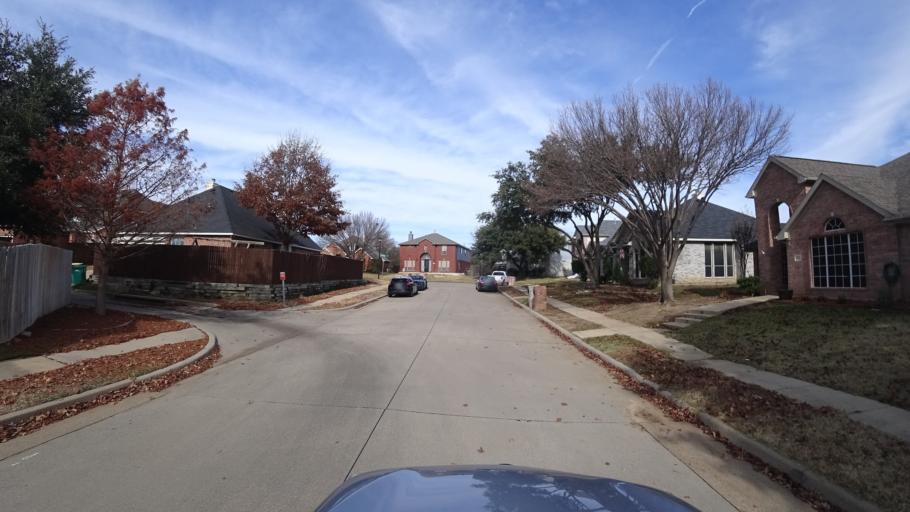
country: US
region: Texas
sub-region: Denton County
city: Highland Village
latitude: 33.0684
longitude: -97.0415
